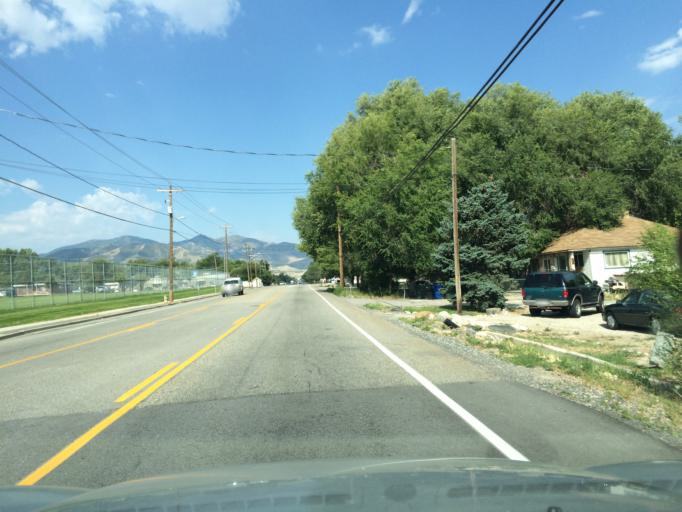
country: US
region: Utah
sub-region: Salt Lake County
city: West Valley City
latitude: 40.6966
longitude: -112.0321
